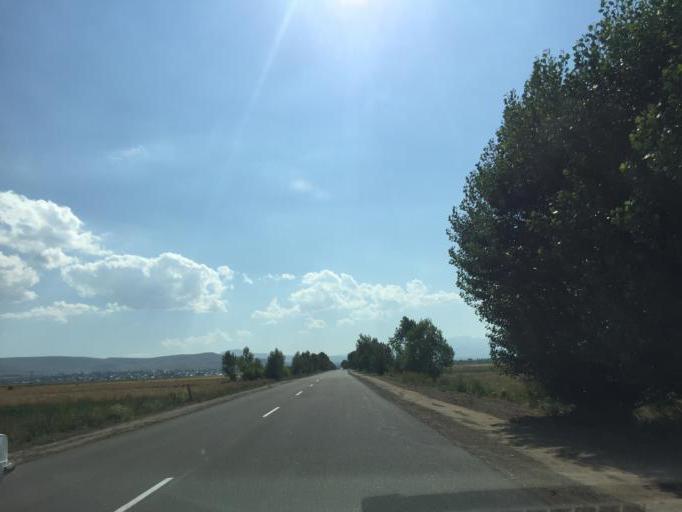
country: AM
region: Geghark'unik'i Marz
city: Vardenik
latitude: 40.1493
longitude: 45.4101
